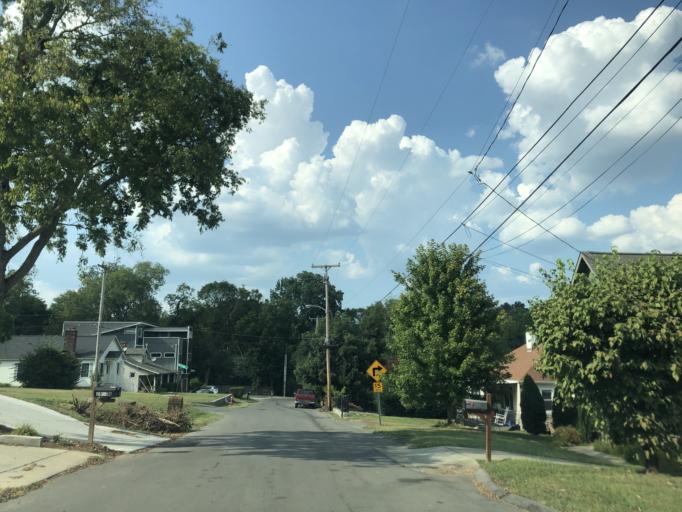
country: US
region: Tennessee
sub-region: Davidson County
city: Oak Hill
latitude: 36.1219
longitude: -86.7812
